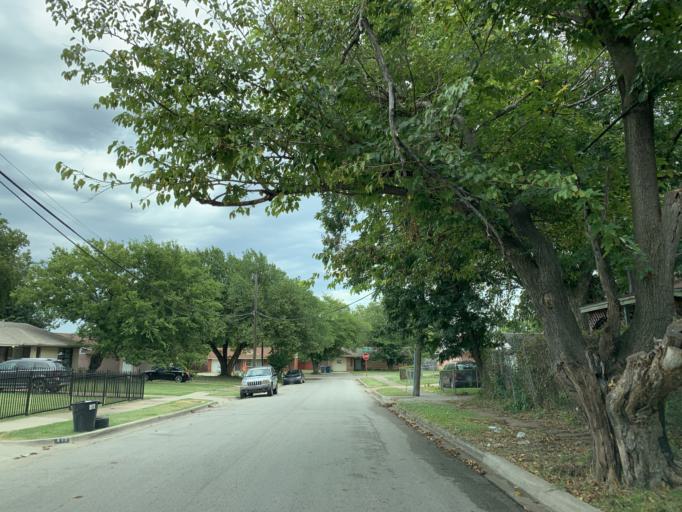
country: US
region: Texas
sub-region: Dallas County
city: DeSoto
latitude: 32.6617
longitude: -96.8276
